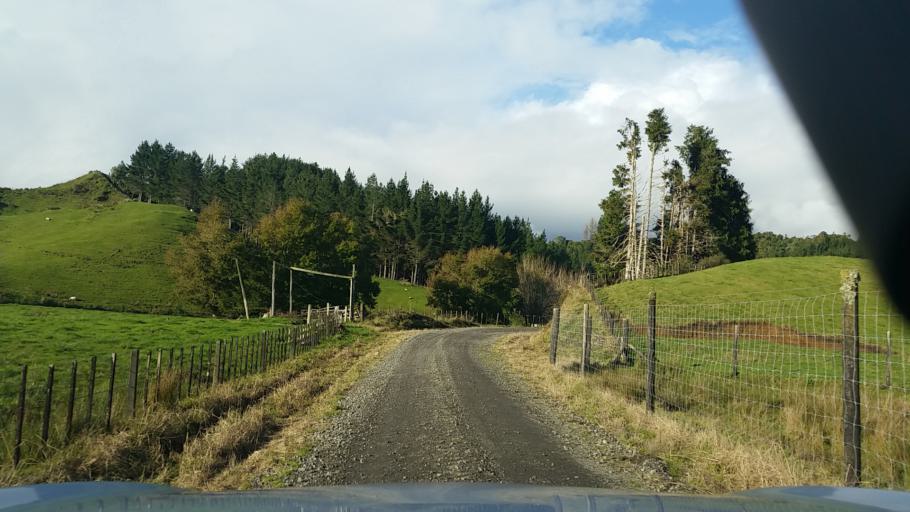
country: NZ
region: Taranaki
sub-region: New Plymouth District
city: Waitara
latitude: -39.1311
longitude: 174.4490
